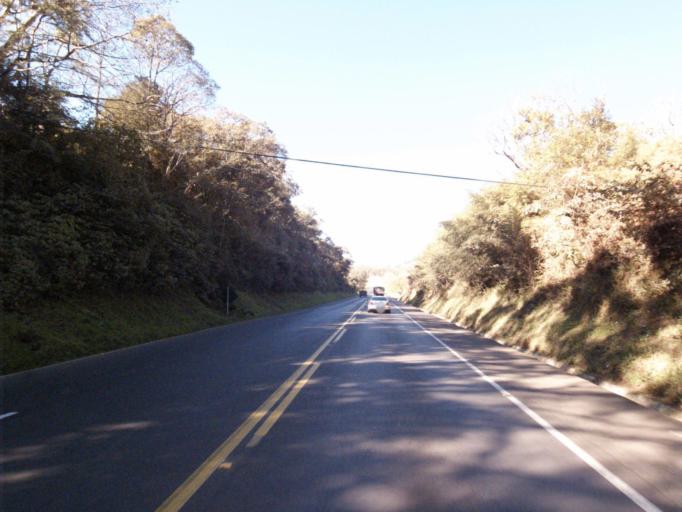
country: BR
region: Santa Catarina
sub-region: Chapeco
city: Chapeco
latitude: -26.9960
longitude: -52.6216
